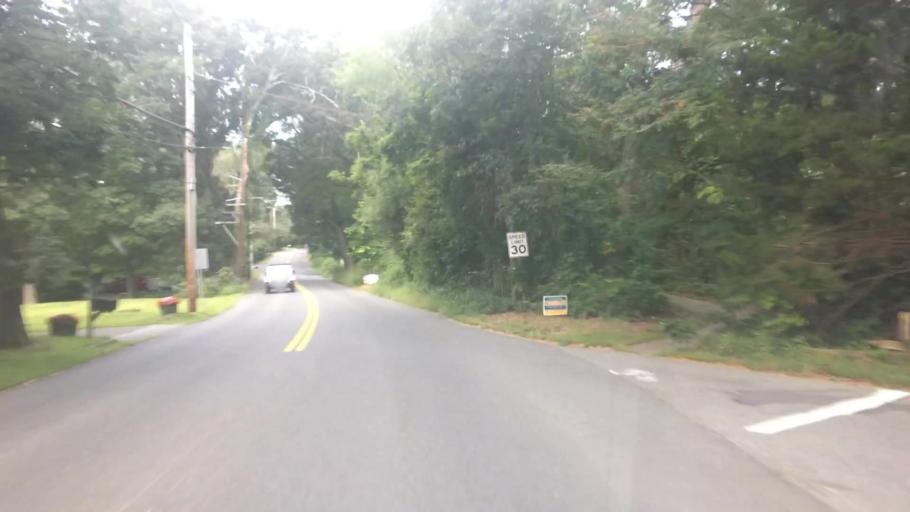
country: US
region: Massachusetts
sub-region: Middlesex County
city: Acton
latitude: 42.4645
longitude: -71.4257
